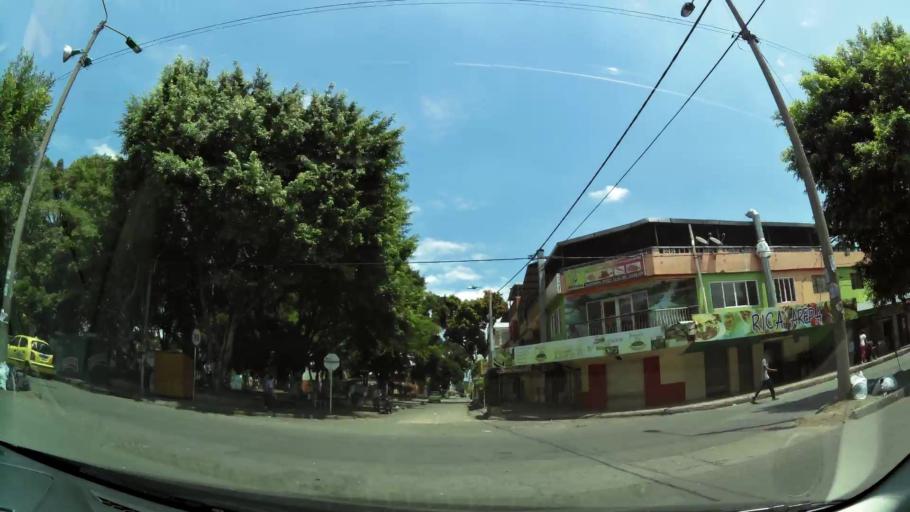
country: CO
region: Valle del Cauca
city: Cali
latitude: 3.4456
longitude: -76.4997
